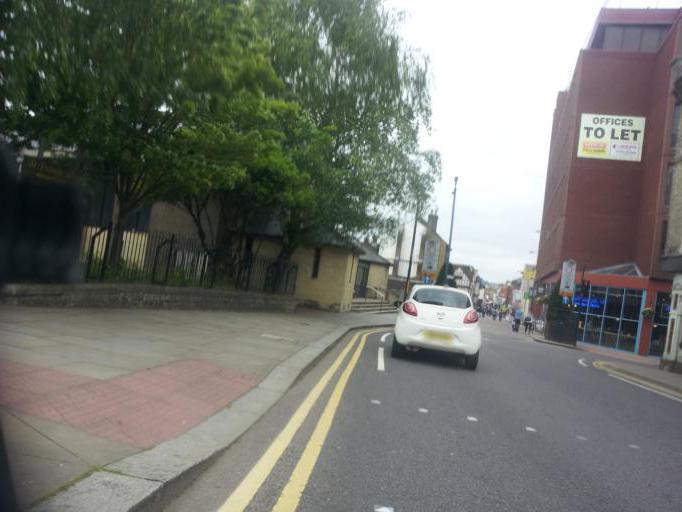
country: GB
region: England
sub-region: Kent
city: Maidstone
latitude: 51.2780
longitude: 0.5218
